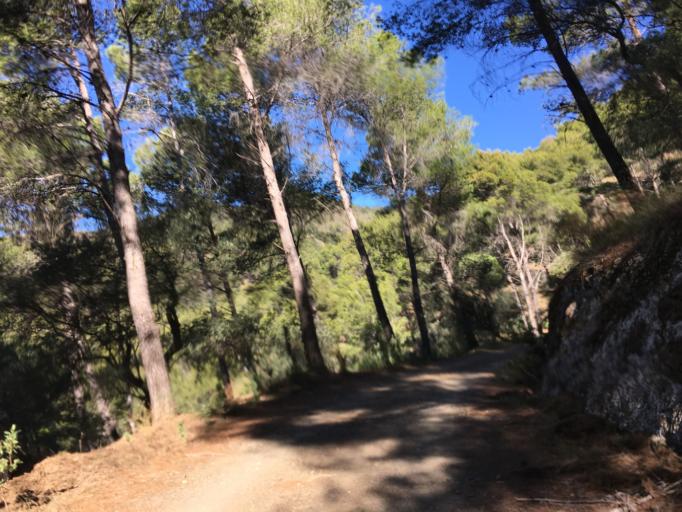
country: ES
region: Andalusia
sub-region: Provincia de Malaga
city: Malaga
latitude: 36.8015
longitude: -4.3993
